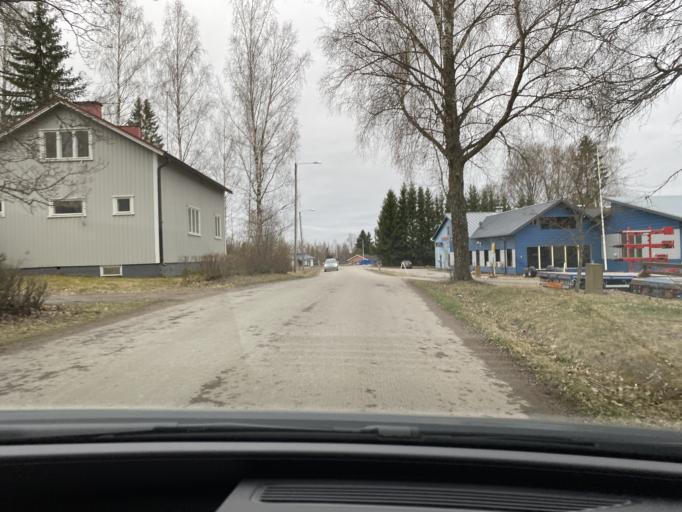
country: FI
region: Satakunta
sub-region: Pori
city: Huittinen
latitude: 61.1921
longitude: 22.7019
